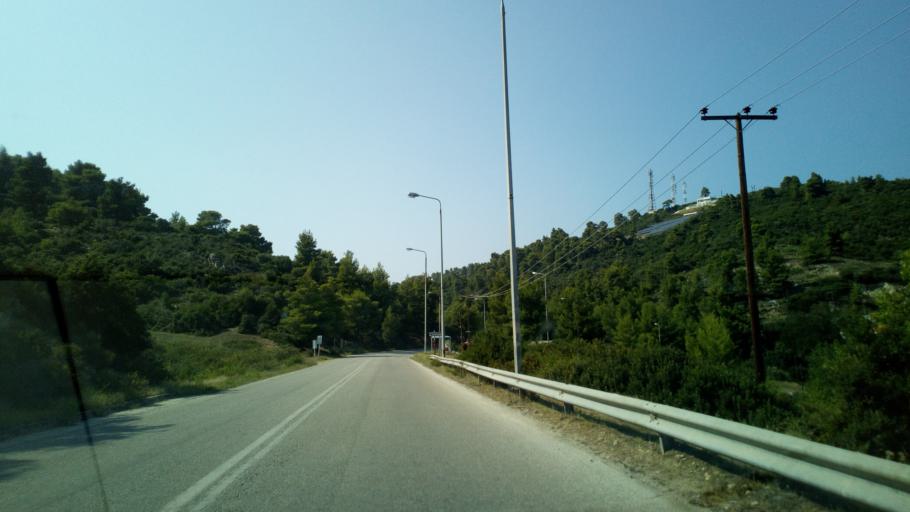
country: GR
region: Central Macedonia
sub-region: Nomos Chalkidikis
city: Sarti
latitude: 40.1023
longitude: 23.9802
